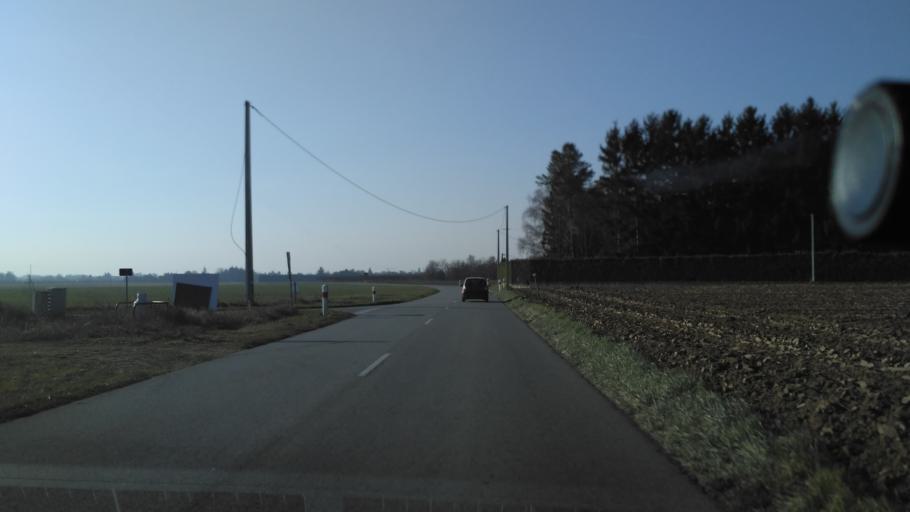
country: FR
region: Rhone-Alpes
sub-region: Departement de la Drome
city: Genissieux
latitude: 45.0710
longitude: 5.0780
